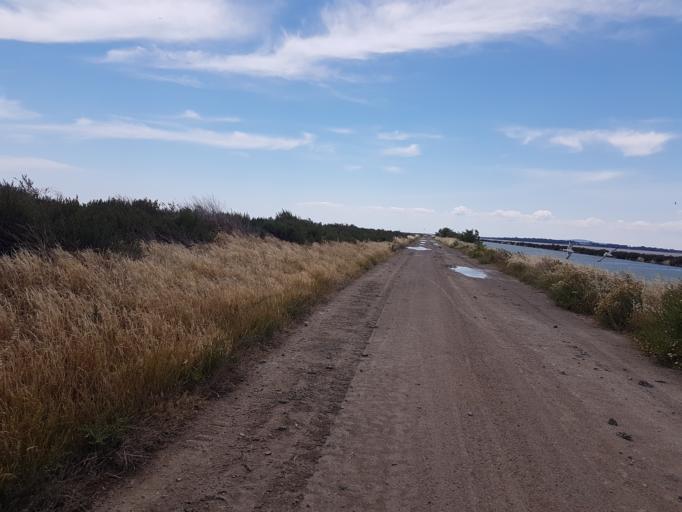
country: FR
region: Languedoc-Roussillon
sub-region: Departement de l'Herault
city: Vic-la-Gardiole
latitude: 43.4877
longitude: 3.8434
